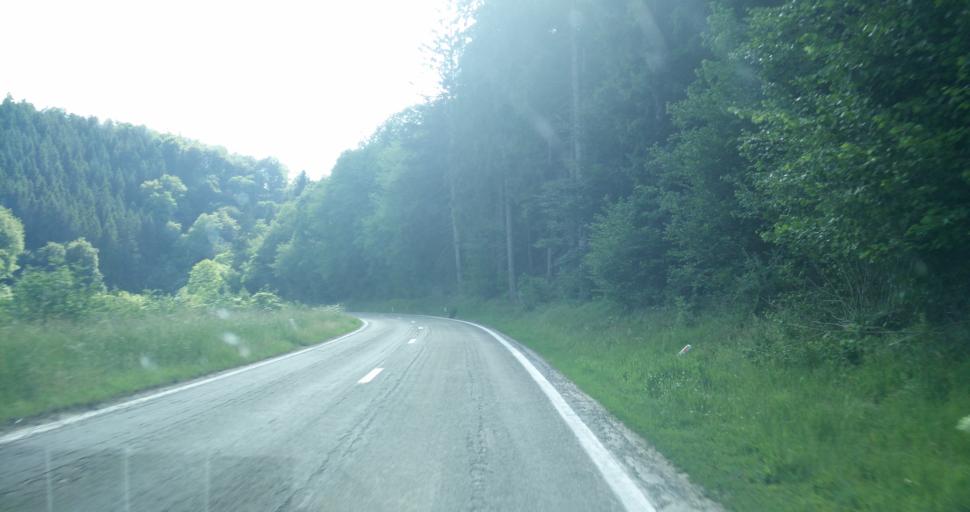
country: BE
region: Wallonia
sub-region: Province du Luxembourg
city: Houffalize
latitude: 50.1321
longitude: 5.7272
